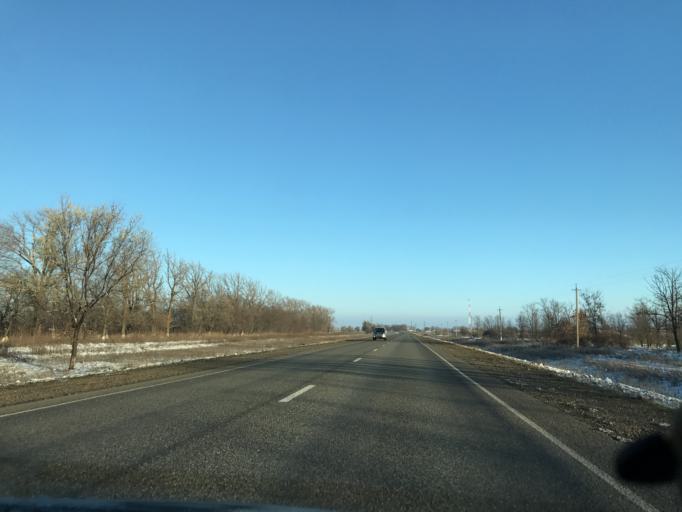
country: RU
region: Stavropol'skiy
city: Bezopasnoye
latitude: 45.6073
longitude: 41.9417
